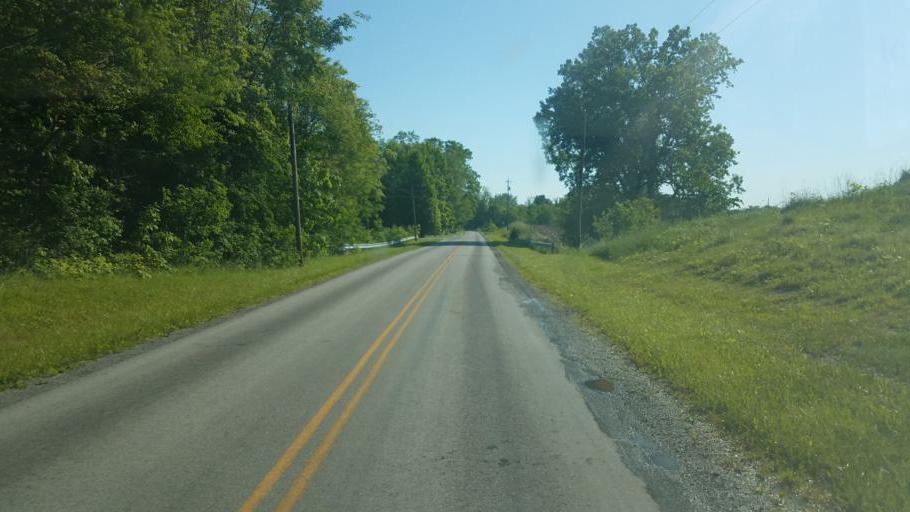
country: US
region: Ohio
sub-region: Hardin County
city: Kenton
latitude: 40.5805
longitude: -83.6282
